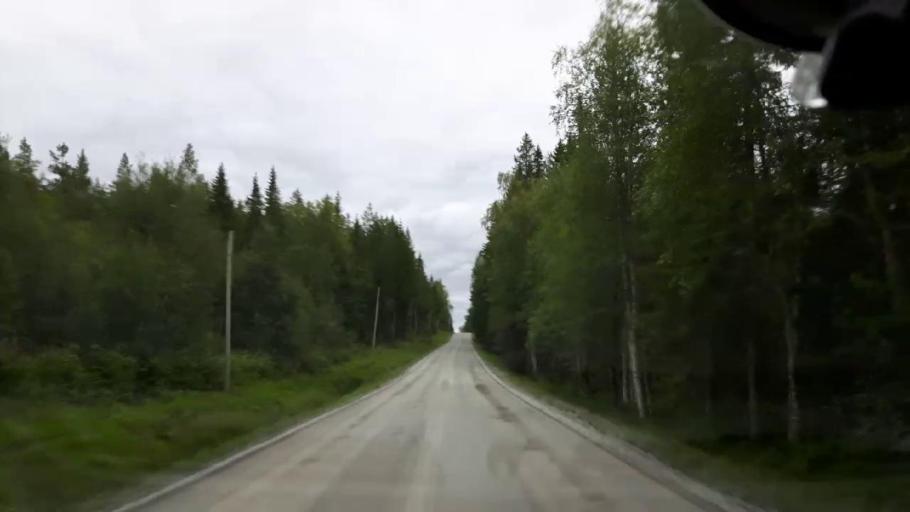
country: SE
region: Jaemtland
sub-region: OEstersunds Kommun
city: Brunflo
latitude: 63.0922
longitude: 15.1400
